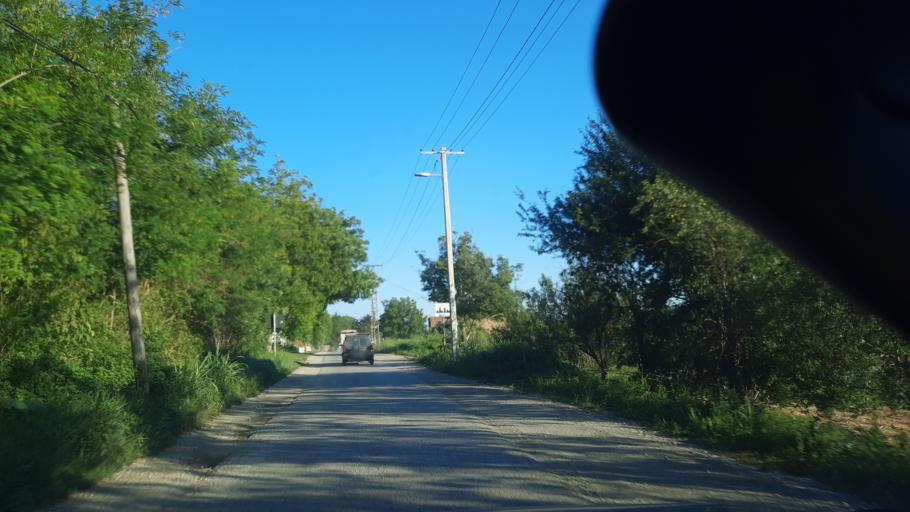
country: RS
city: Cortanovci
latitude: 45.1189
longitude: 19.9447
